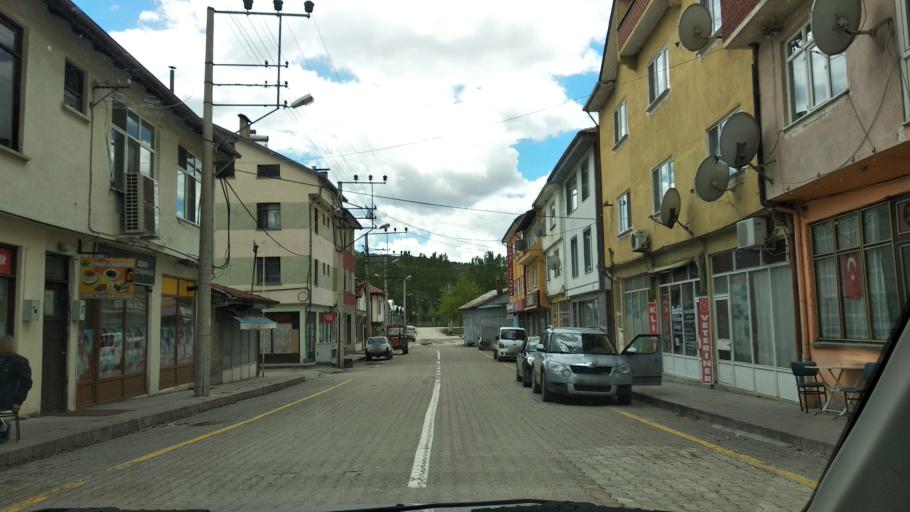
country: TR
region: Bolu
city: Seben
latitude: 40.4088
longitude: 31.5706
